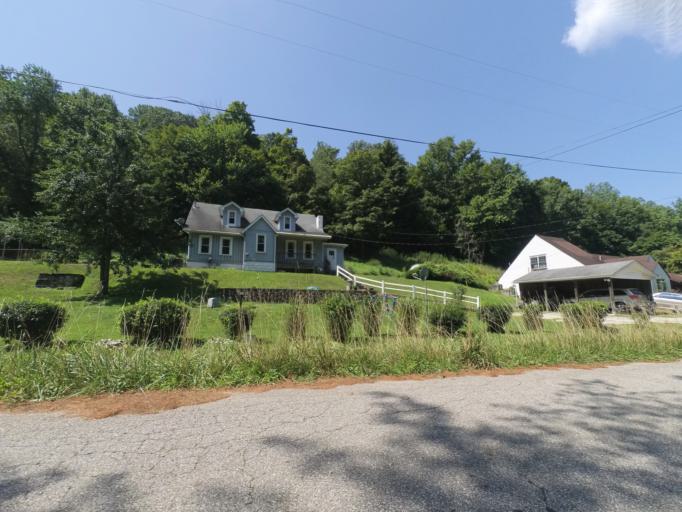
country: US
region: West Virginia
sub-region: Cabell County
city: Huntington
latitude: 38.3873
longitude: -82.4495
